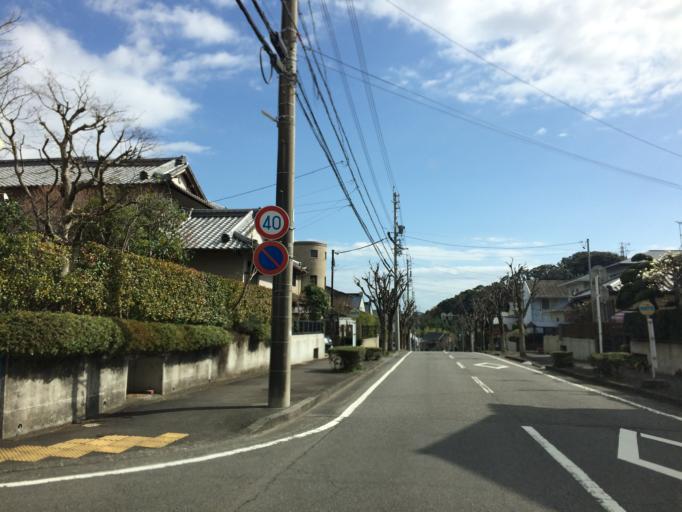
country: JP
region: Shizuoka
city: Fujieda
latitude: 34.8590
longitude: 138.2327
